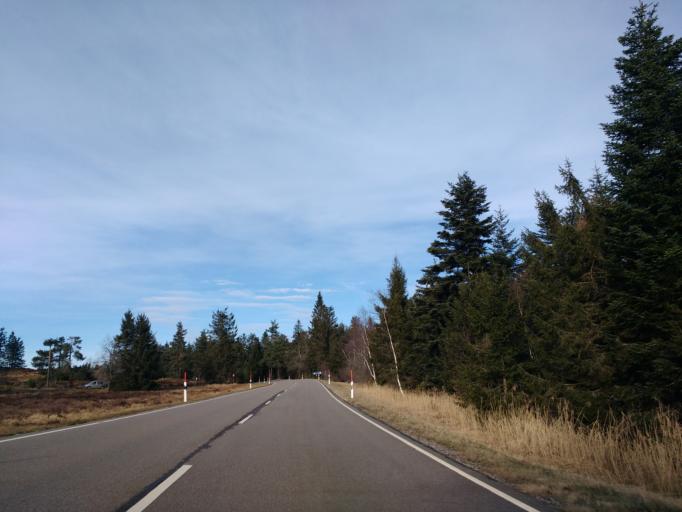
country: DE
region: Baden-Wuerttemberg
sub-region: Freiburg Region
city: Bad Peterstal-Griesbach
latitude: 48.4986
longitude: 8.2365
